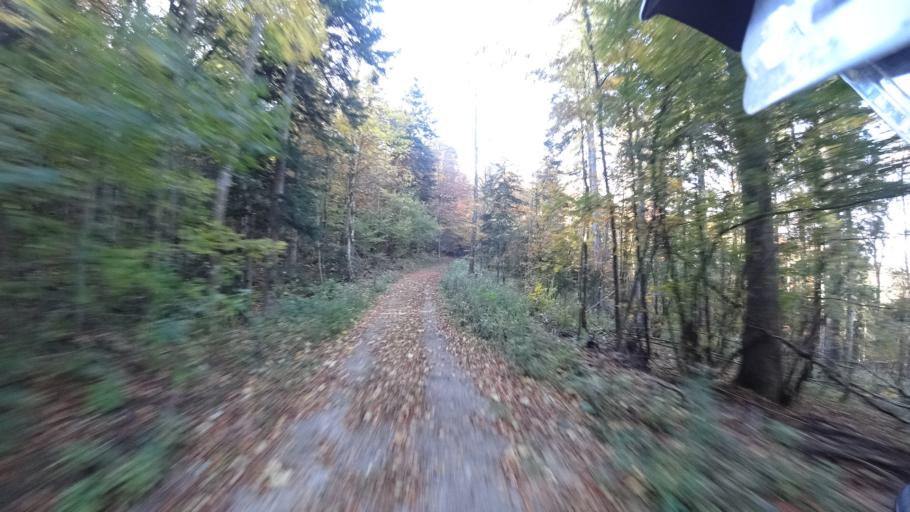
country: HR
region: Karlovacka
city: Plaski
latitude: 45.0066
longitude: 15.3913
